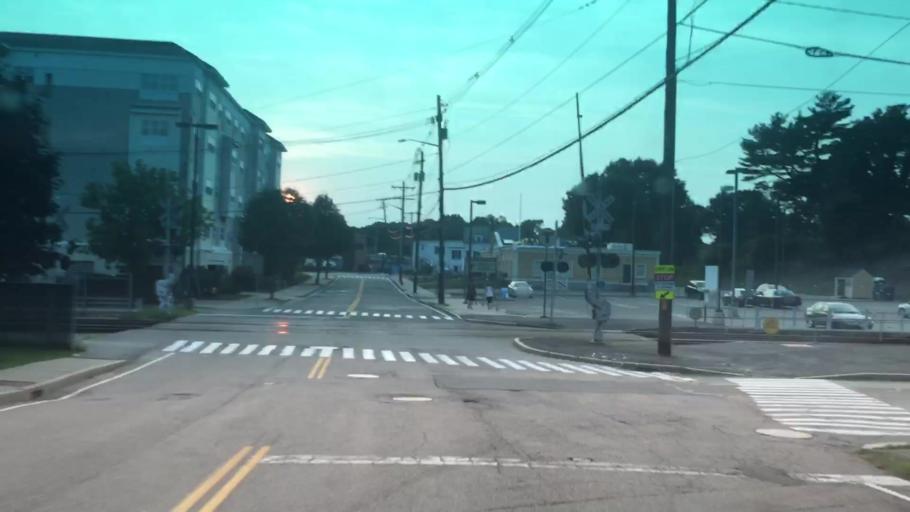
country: US
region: Massachusetts
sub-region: Norfolk County
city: Norwood
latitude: 42.1956
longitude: -71.1963
